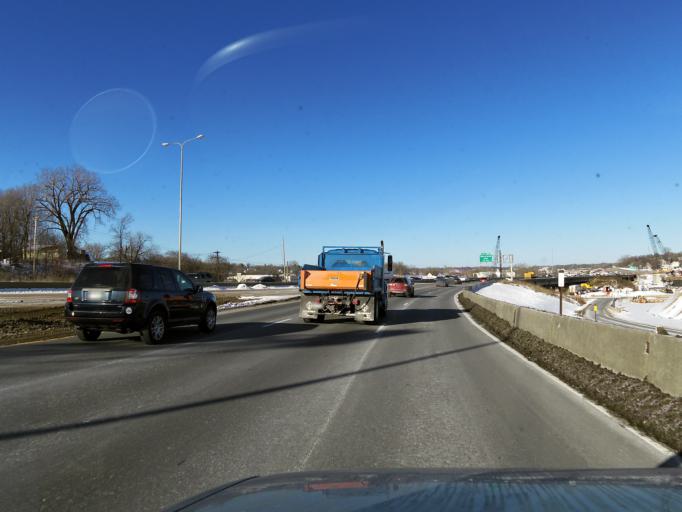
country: US
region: Minnesota
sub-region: Ramsey County
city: Saint Paul
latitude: 44.9651
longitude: -93.0905
